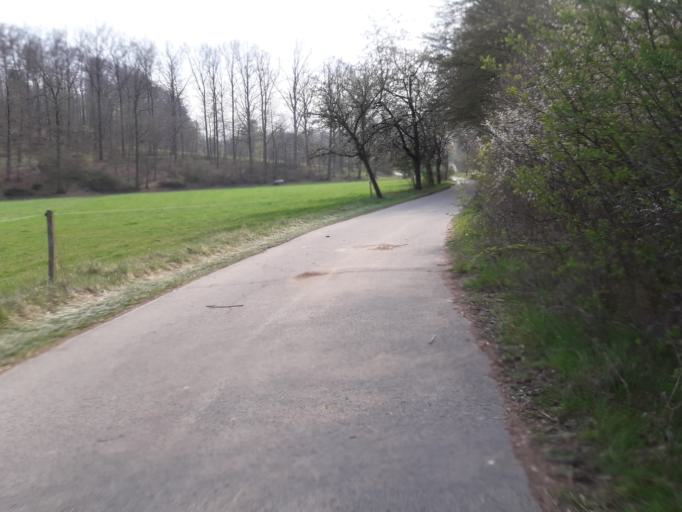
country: DE
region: North Rhine-Westphalia
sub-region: Regierungsbezirk Detmold
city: Paderborn
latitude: 51.6700
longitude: 8.7793
